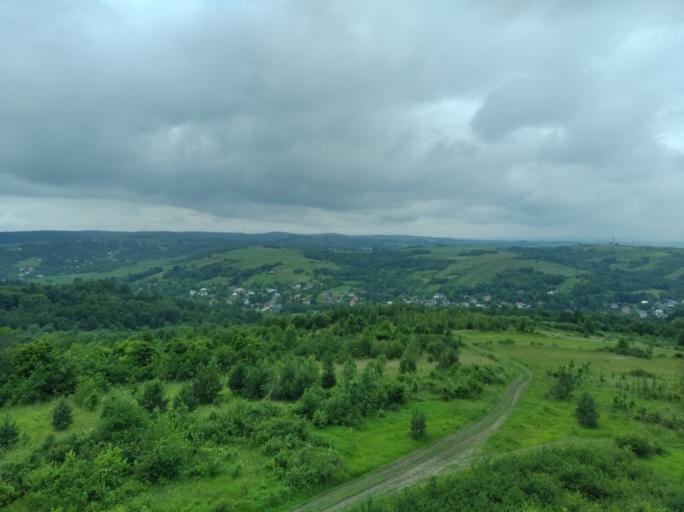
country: PL
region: Subcarpathian Voivodeship
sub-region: Powiat jaroslawski
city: Pruchnik
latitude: 49.8889
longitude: 22.5121
